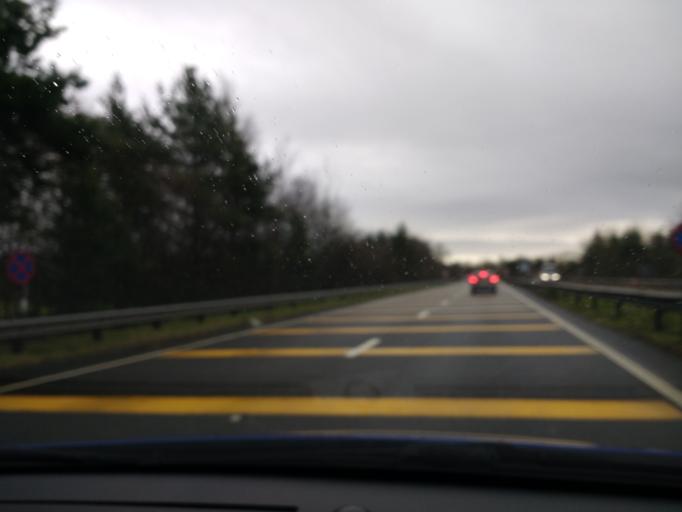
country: GB
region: England
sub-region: Cumbria
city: Milnthorpe
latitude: 54.2376
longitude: -2.7202
